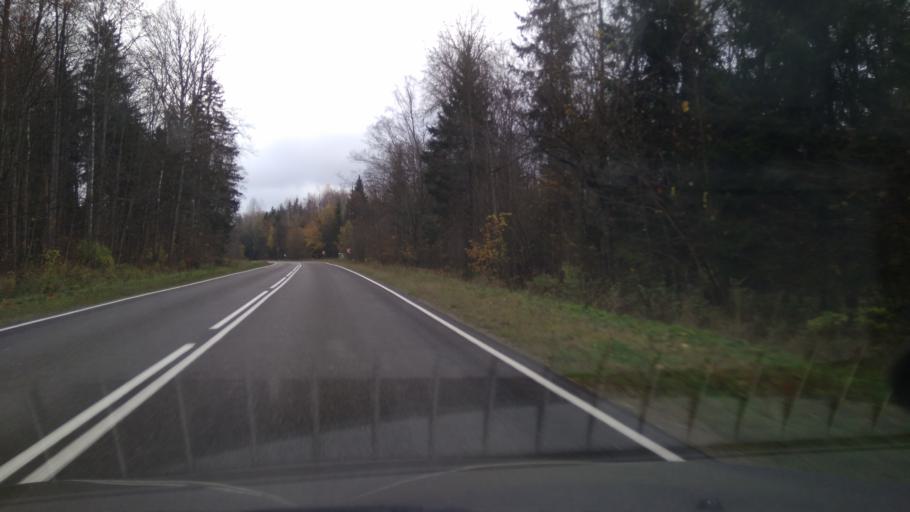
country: BY
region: Minsk
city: Urechcha
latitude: 53.2080
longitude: 27.9142
